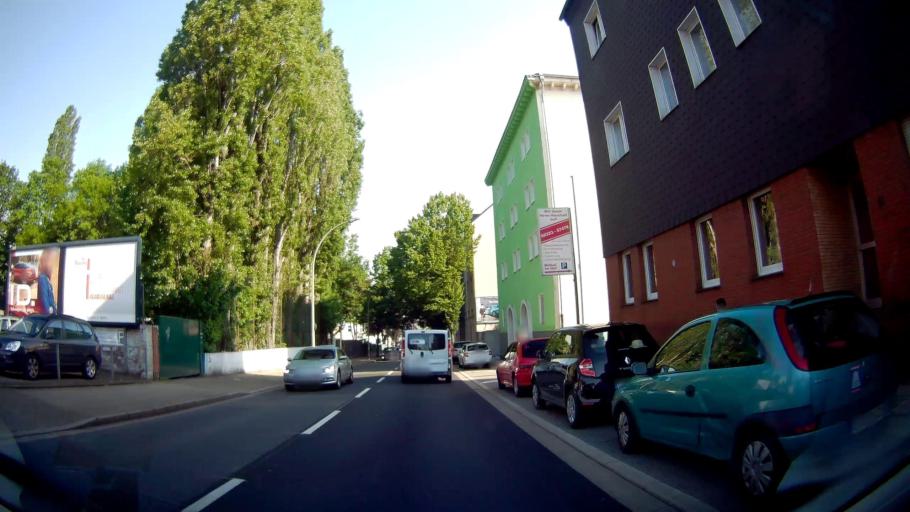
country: DE
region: North Rhine-Westphalia
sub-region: Regierungsbezirk Arnsberg
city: Herne
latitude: 51.5385
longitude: 7.2287
